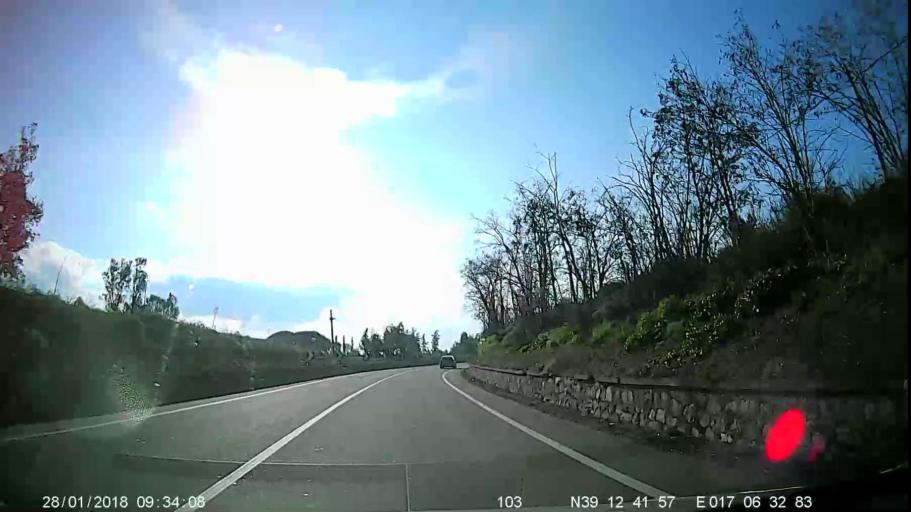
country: IT
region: Calabria
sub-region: Provincia di Crotone
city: Tronca
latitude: 39.2112
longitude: 17.1093
